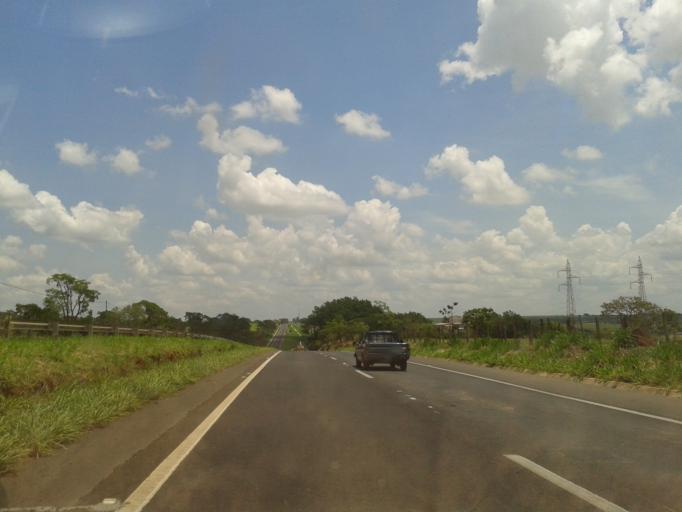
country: BR
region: Minas Gerais
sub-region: Uberlandia
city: Uberlandia
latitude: -18.8703
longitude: -48.5534
